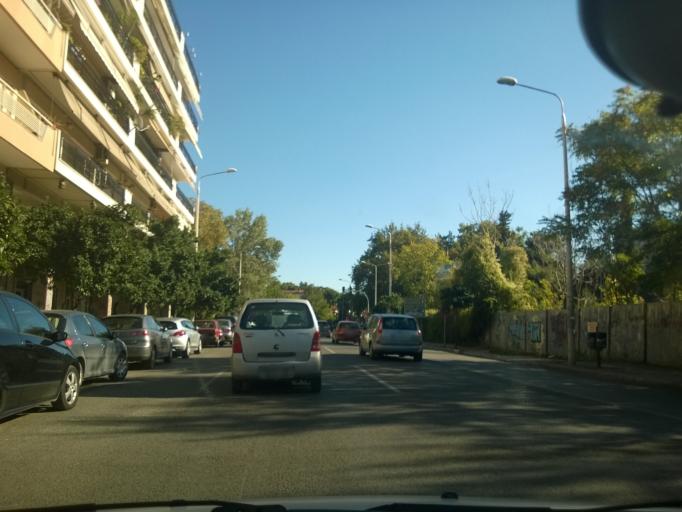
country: GR
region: Central Macedonia
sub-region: Nomos Thessalonikis
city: Kalamaria
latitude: 40.5960
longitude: 22.9533
